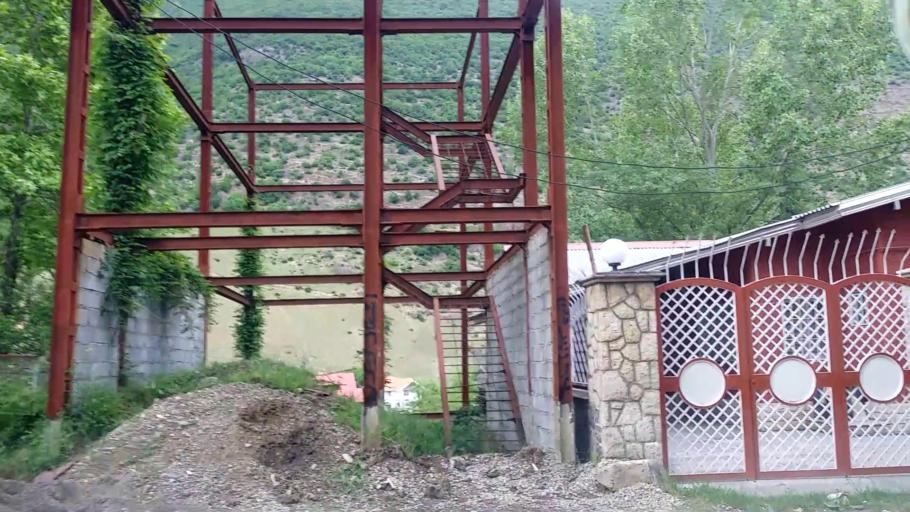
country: IR
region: Mazandaran
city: `Abbasabad
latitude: 36.4933
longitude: 51.1350
